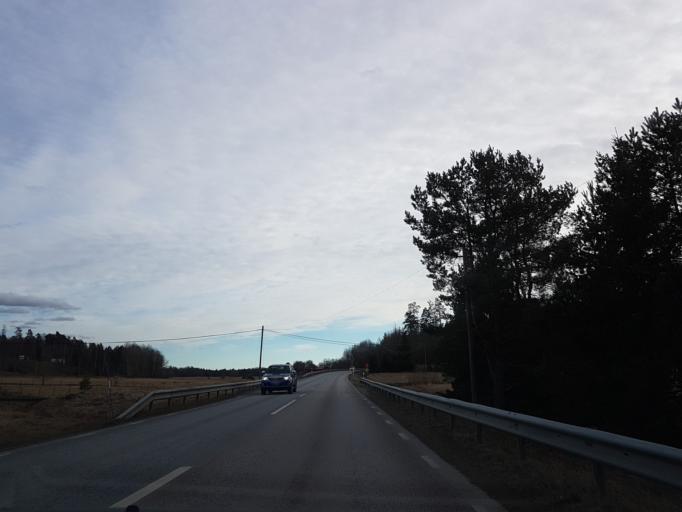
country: SE
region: Stockholm
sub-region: Vallentuna Kommun
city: Vallentuna
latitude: 59.6621
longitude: 18.0469
